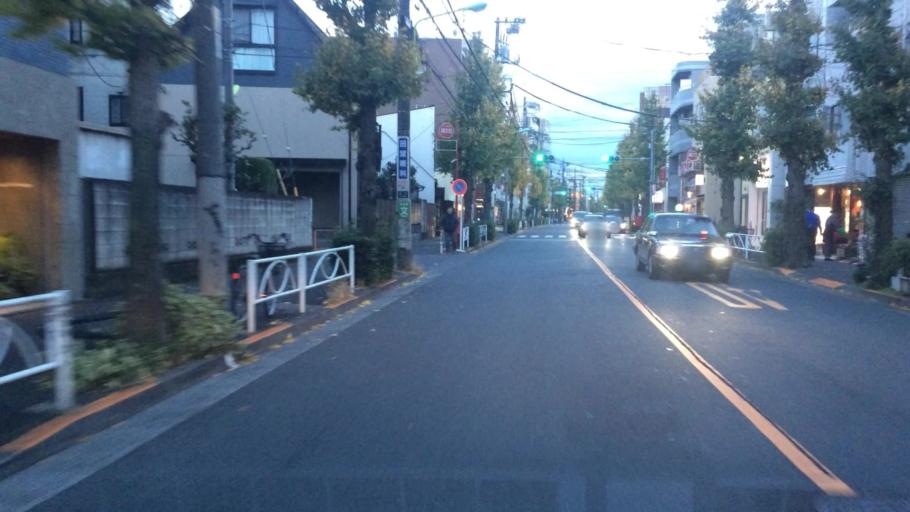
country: JP
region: Tokyo
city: Tokyo
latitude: 35.6268
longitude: 139.6560
